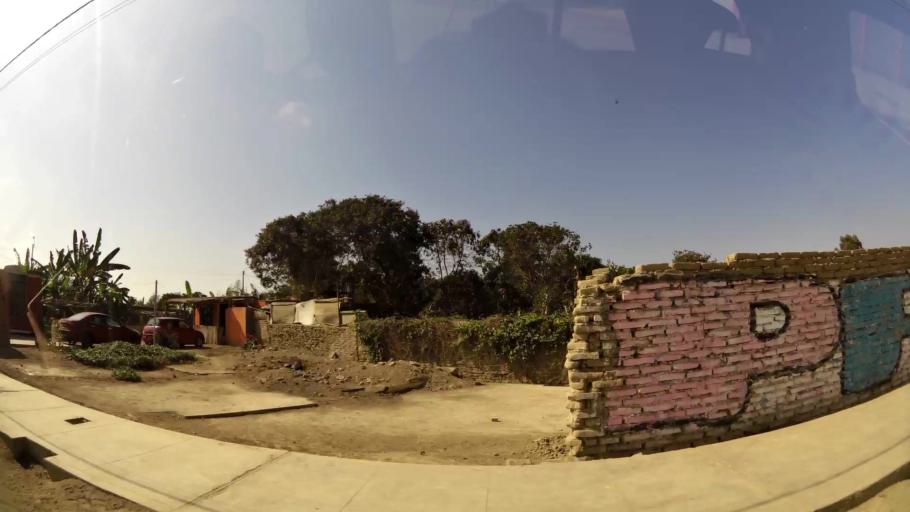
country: PE
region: Ica
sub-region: Provincia de Chincha
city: Sunampe
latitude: -13.4258
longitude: -76.1656
